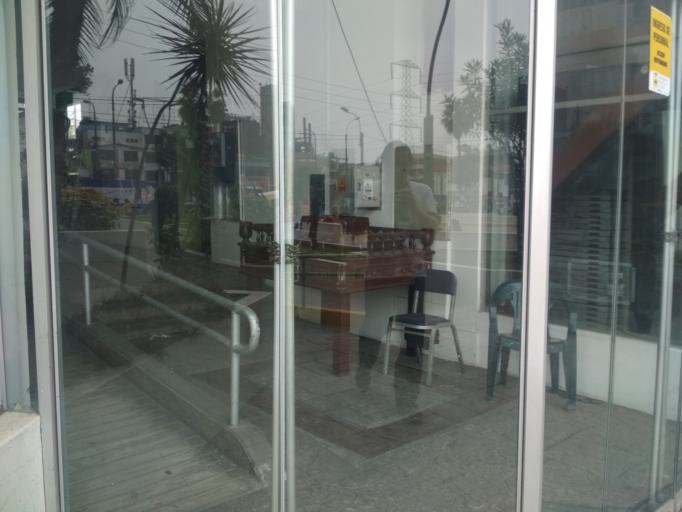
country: PE
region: Lima
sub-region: Lima
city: Independencia
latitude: -11.9914
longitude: -77.0708
